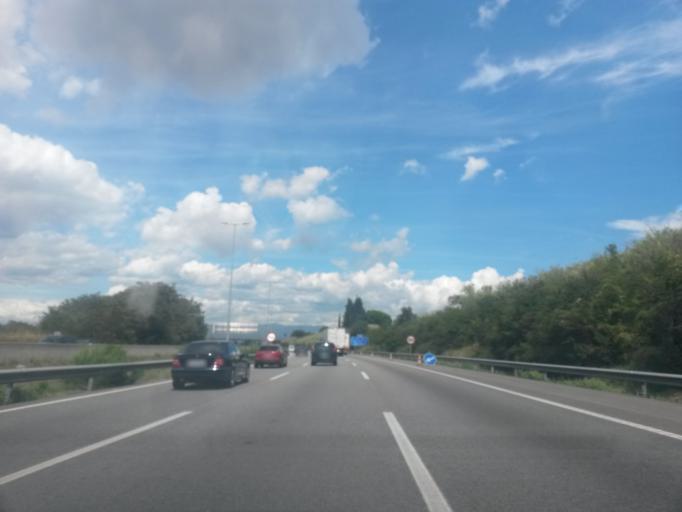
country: ES
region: Catalonia
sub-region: Provincia de Barcelona
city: Granollers
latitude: 41.5708
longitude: 2.2838
